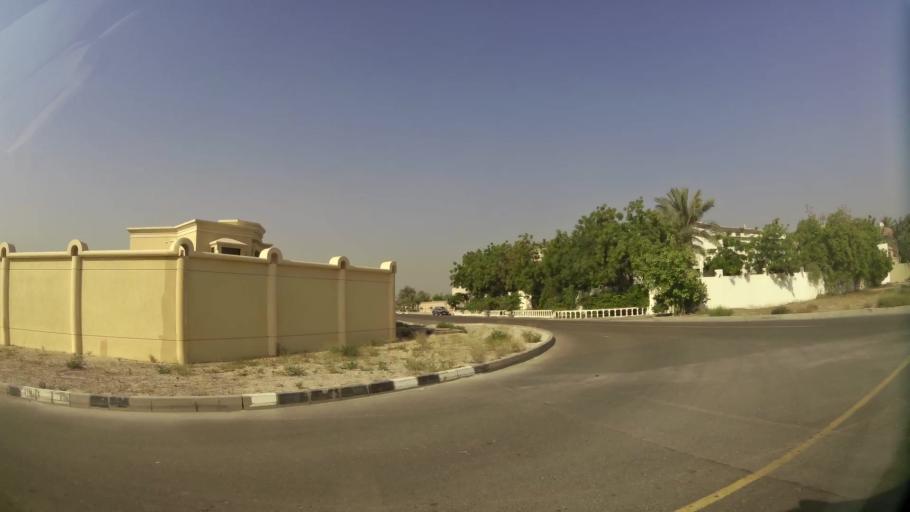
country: AE
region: Ash Shariqah
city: Sharjah
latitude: 25.3097
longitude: 55.3446
